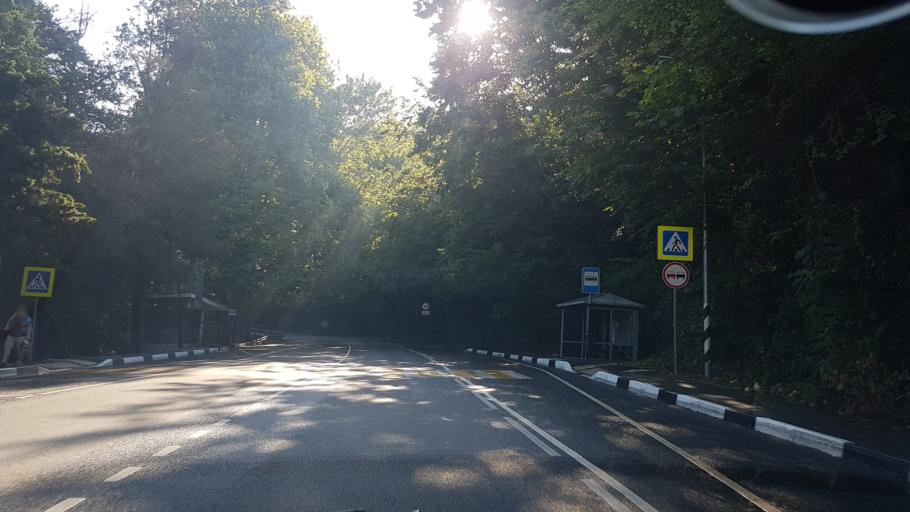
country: RU
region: Krasnodarskiy
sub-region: Sochi City
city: Lazarevskoye
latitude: 43.8588
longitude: 39.4032
